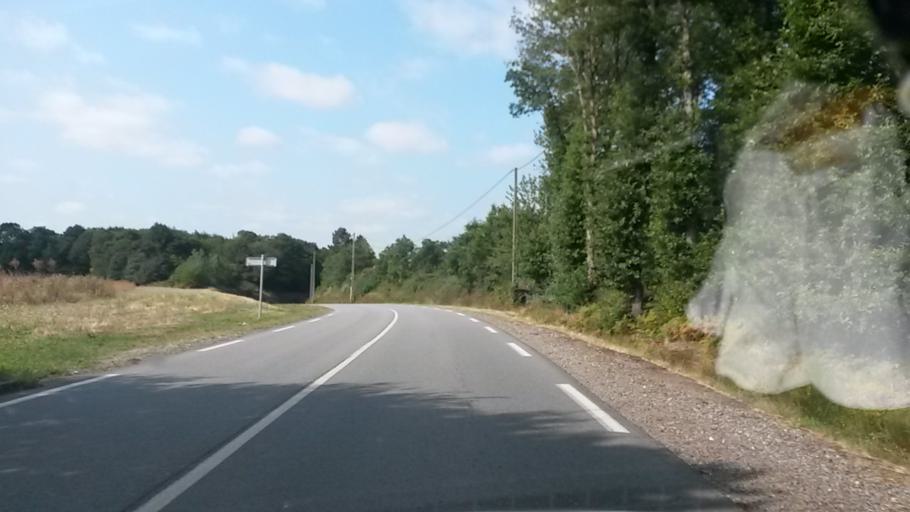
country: FR
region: Haute-Normandie
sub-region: Departement de l'Eure
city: Damville
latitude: 48.8487
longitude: 1.0531
